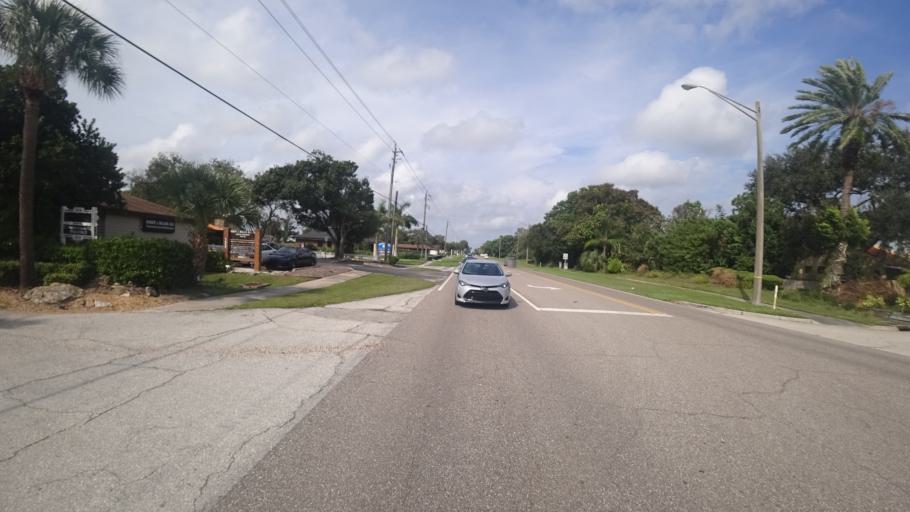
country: US
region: Florida
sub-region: Manatee County
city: West Bradenton
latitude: 27.4869
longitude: -82.6205
